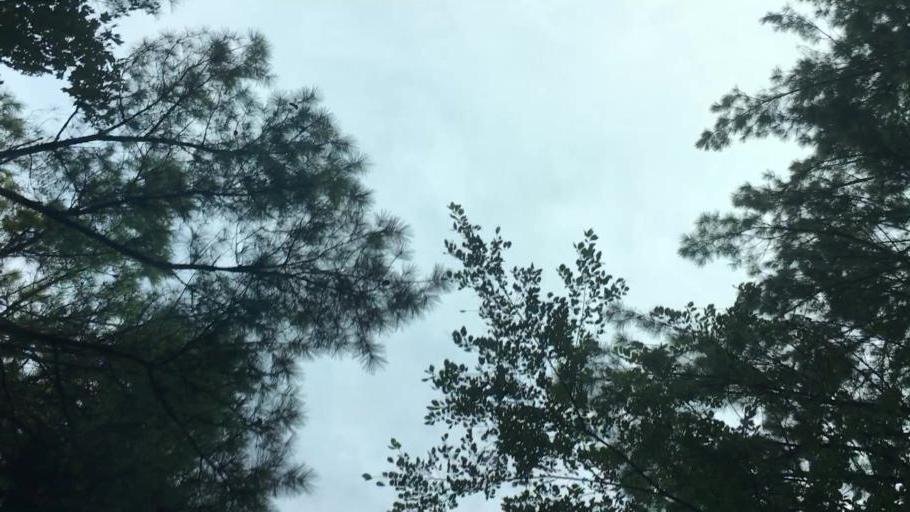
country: US
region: Alabama
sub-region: Bibb County
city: Woodstock
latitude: 33.2355
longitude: -87.1451
